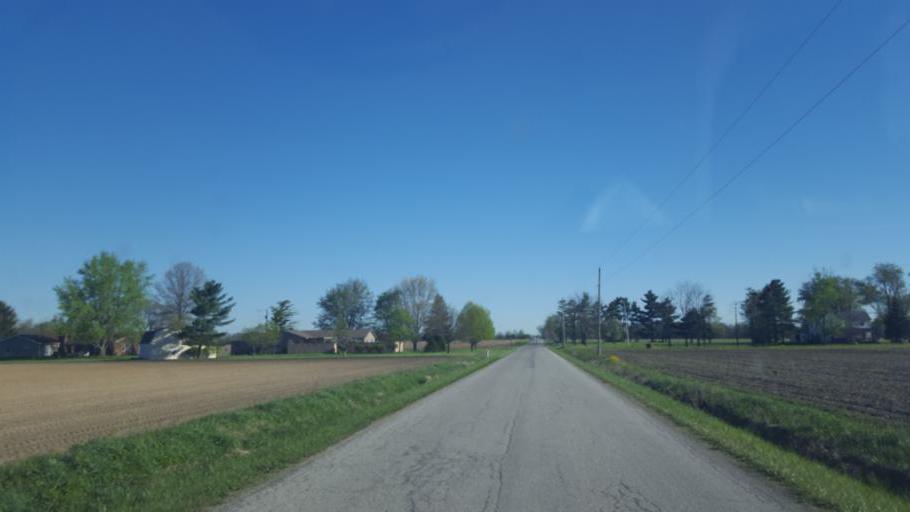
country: US
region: Ohio
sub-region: Morrow County
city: Mount Gilead
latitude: 40.6148
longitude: -82.9184
